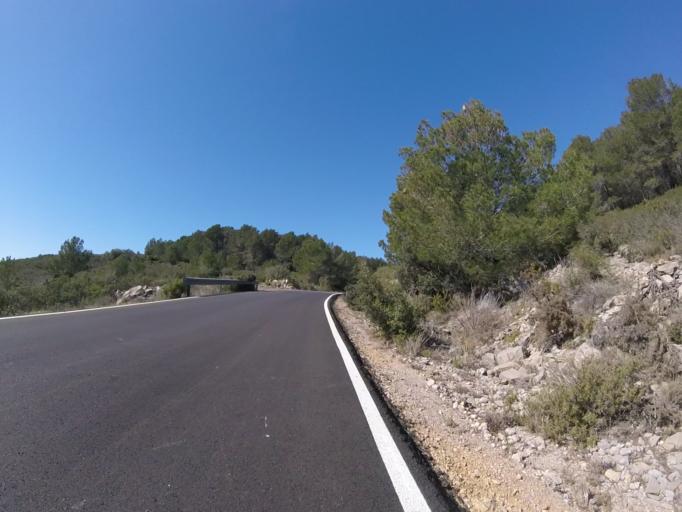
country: ES
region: Valencia
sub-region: Provincia de Castello
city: Cervera del Maestre
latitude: 40.4073
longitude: 0.1979
